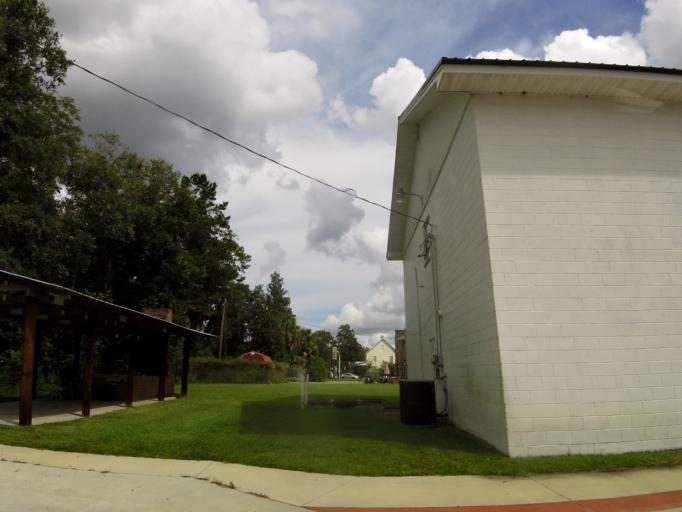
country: US
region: Georgia
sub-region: Brantley County
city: Nahunta
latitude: 31.2049
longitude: -81.9824
